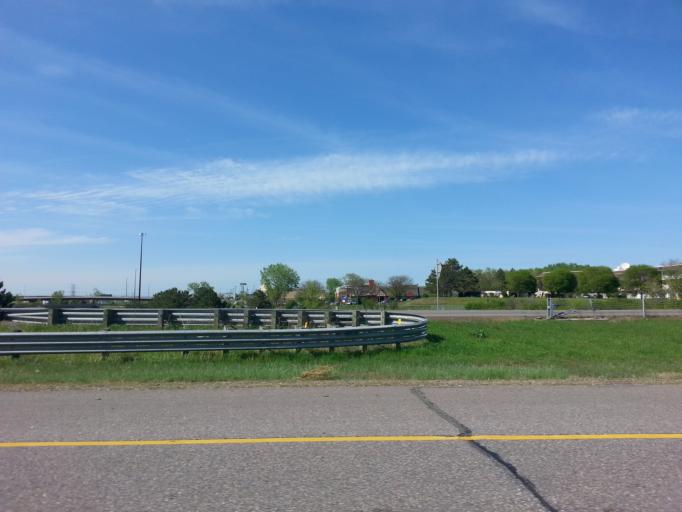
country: US
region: Minnesota
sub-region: Ramsey County
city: Lauderdale
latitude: 45.0100
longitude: -93.1856
